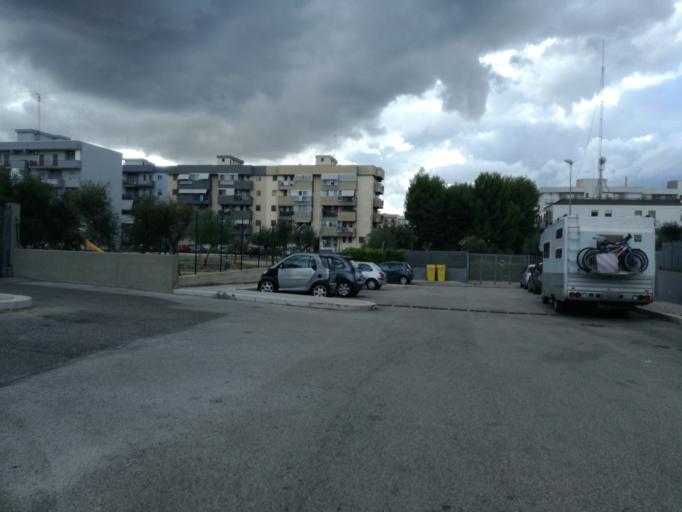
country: IT
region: Apulia
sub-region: Provincia di Bari
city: Triggiano
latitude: 41.0703
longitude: 16.9323
